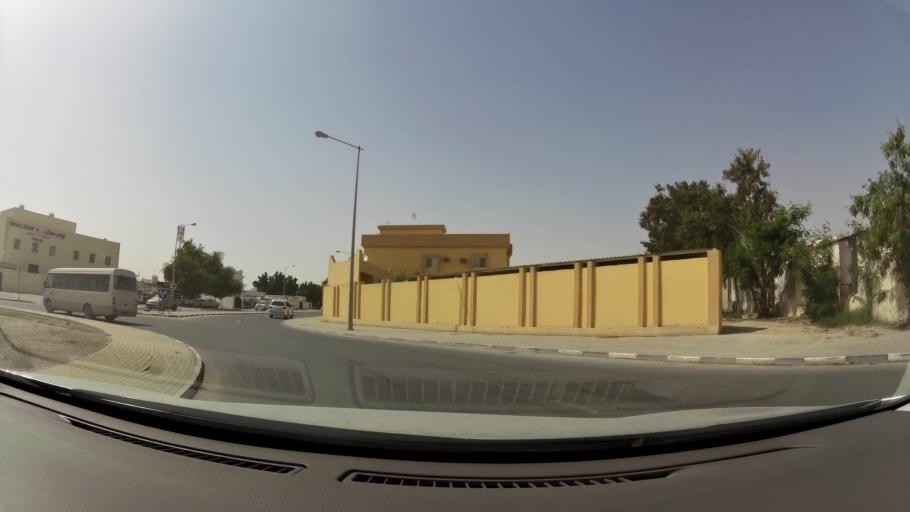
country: QA
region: Baladiyat Umm Salal
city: Umm Salal Muhammad
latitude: 25.3985
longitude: 51.4248
